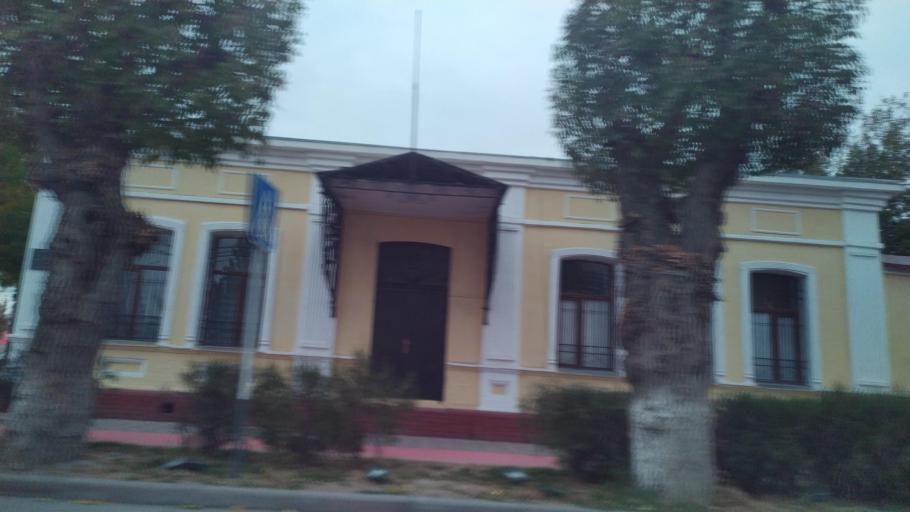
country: KZ
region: Ongtustik Qazaqstan
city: Turkestan
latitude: 43.3000
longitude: 68.2755
